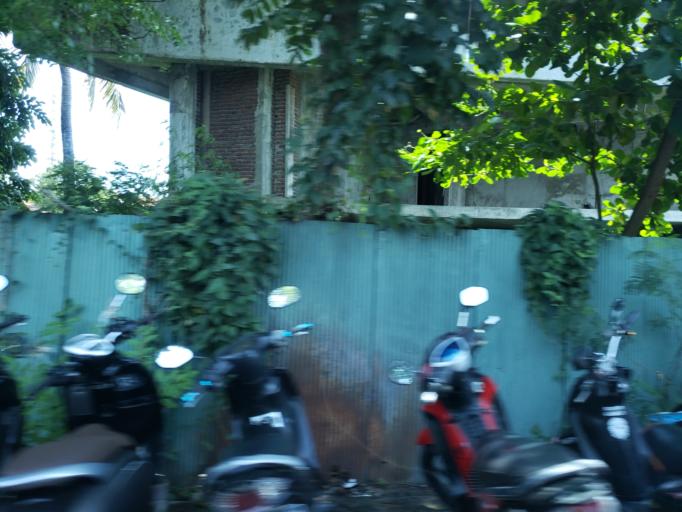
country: ID
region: Bali
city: Jimbaran
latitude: -8.7813
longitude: 115.1641
